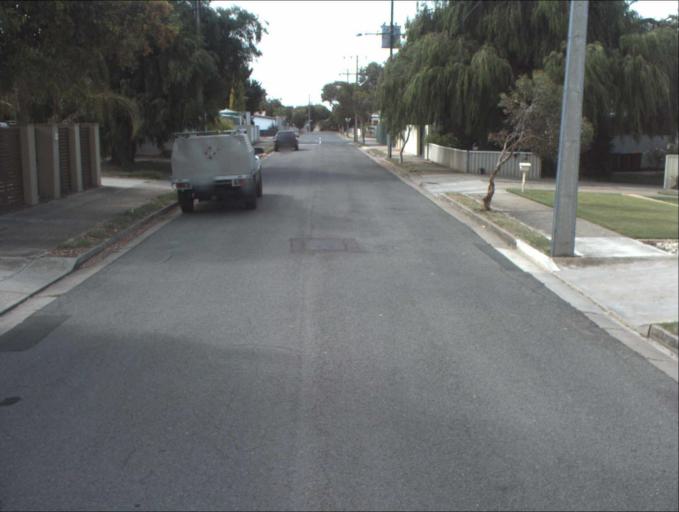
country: AU
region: South Australia
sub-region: Port Adelaide Enfield
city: Birkenhead
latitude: -34.8020
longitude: 138.4957
